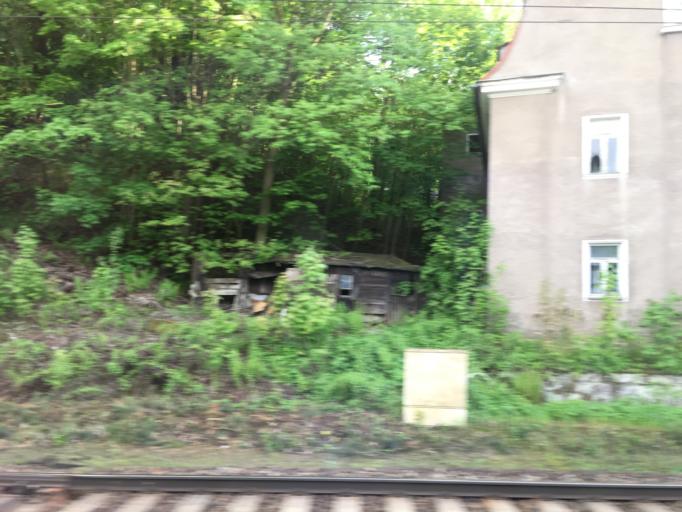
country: DE
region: Saxony
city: Rathmannsdorf
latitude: 50.9218
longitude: 14.1282
